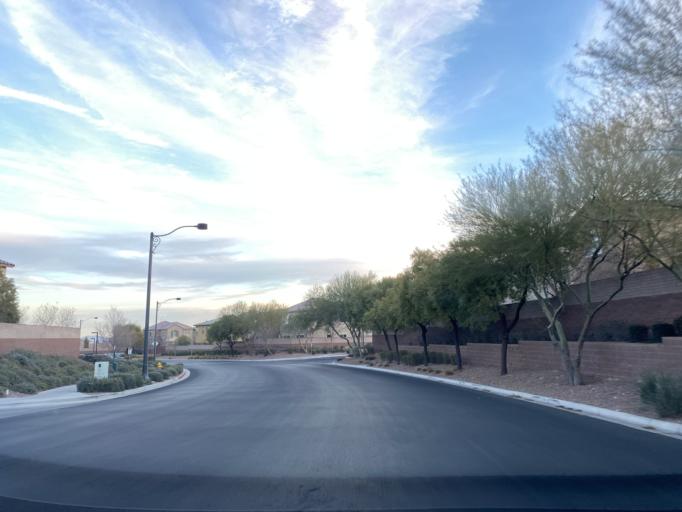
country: US
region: Nevada
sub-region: Clark County
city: Summerlin South
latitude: 36.3013
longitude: -115.3259
